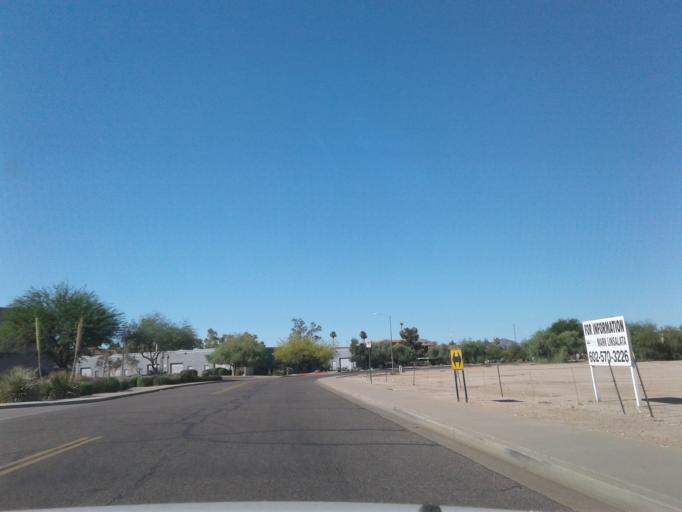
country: US
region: Arizona
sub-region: Maricopa County
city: Paradise Valley
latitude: 33.6203
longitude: -111.9092
